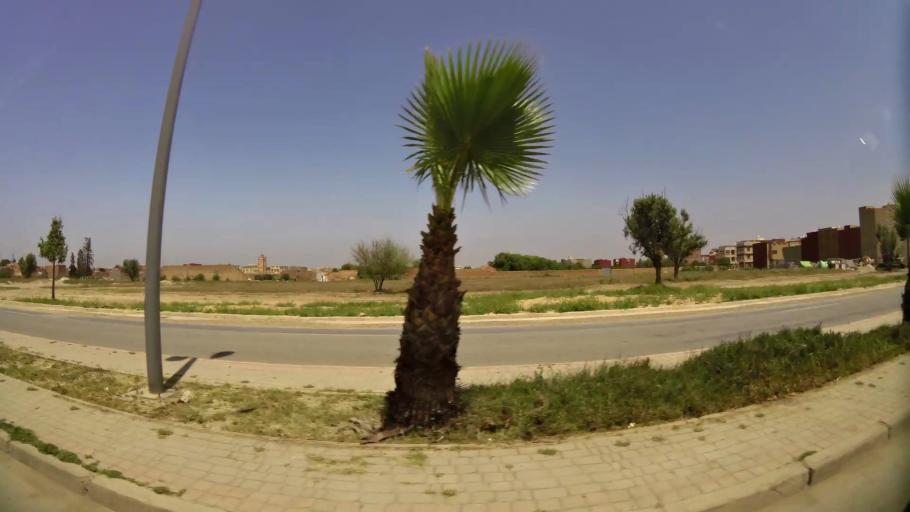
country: MA
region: Oriental
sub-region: Oujda-Angad
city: Oujda
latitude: 34.6915
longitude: -1.8957
